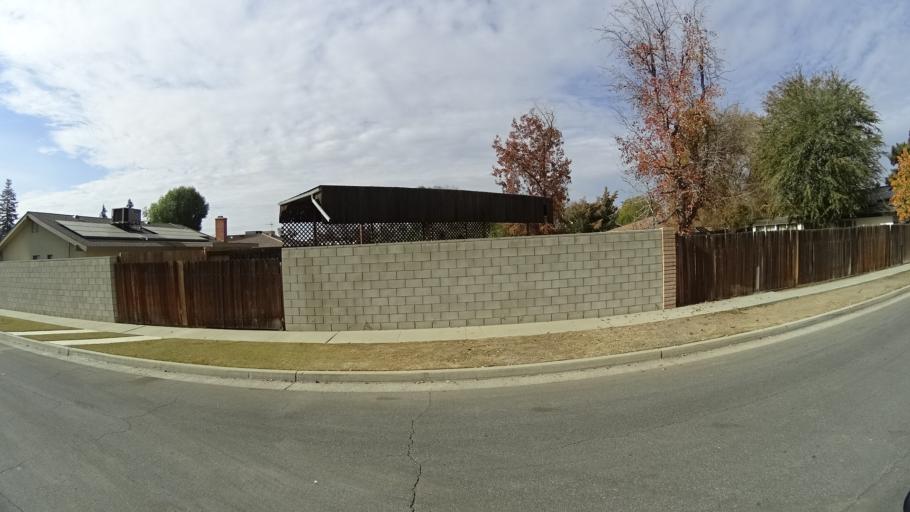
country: US
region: California
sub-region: Kern County
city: Greenacres
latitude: 35.4098
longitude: -119.0900
